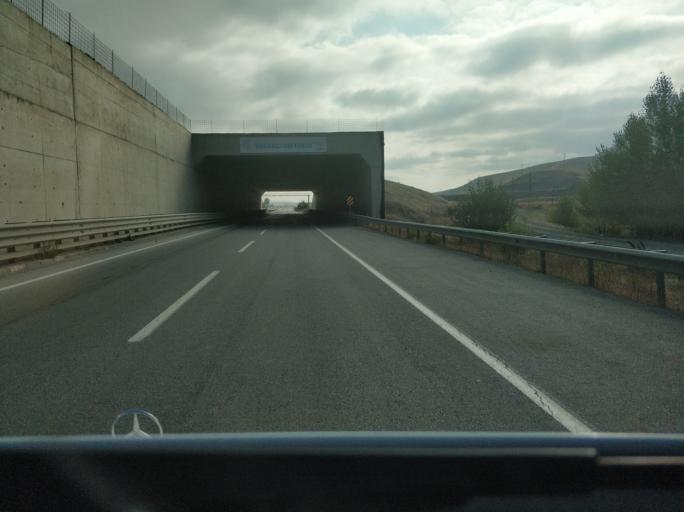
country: TR
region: Sivas
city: Yildizeli
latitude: 39.8544
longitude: 36.5413
